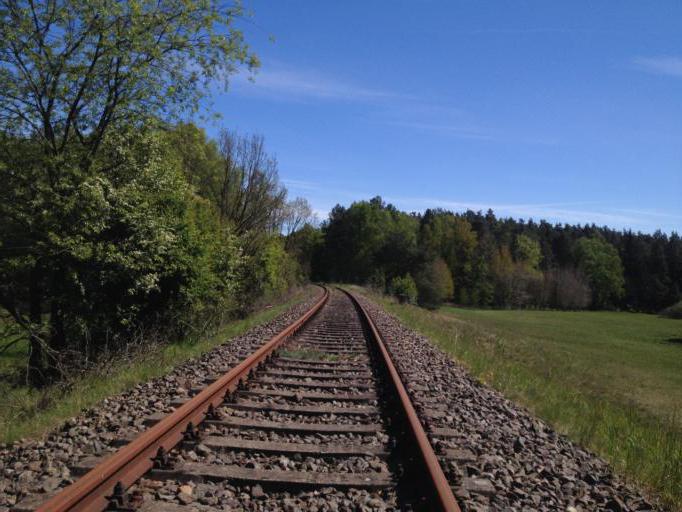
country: DE
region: Brandenburg
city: Lychen
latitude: 53.1537
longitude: 13.3946
